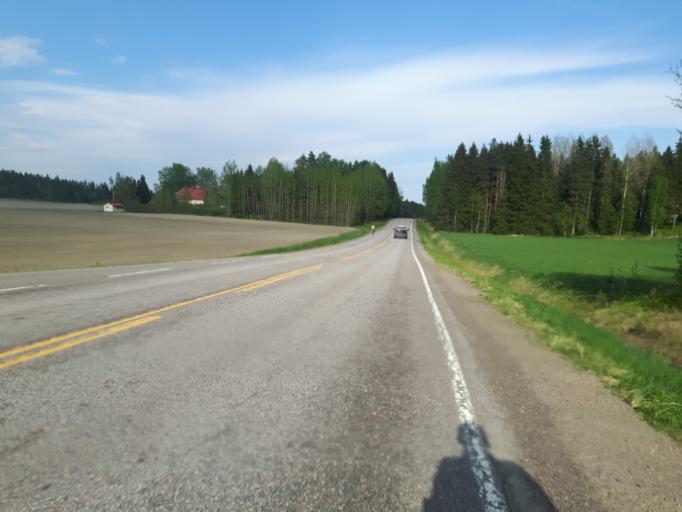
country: FI
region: Uusimaa
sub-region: Porvoo
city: Myrskylae
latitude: 60.4824
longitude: 25.8342
